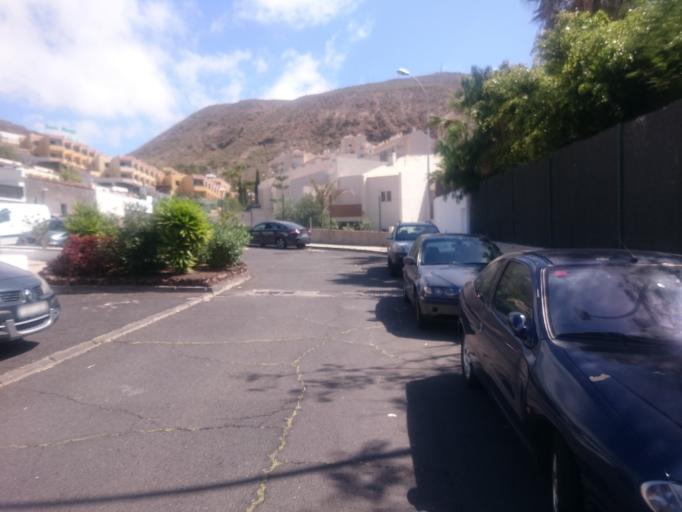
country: ES
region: Canary Islands
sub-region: Provincia de Santa Cruz de Tenerife
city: Playa de las Americas
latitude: 28.0560
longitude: -16.7062
